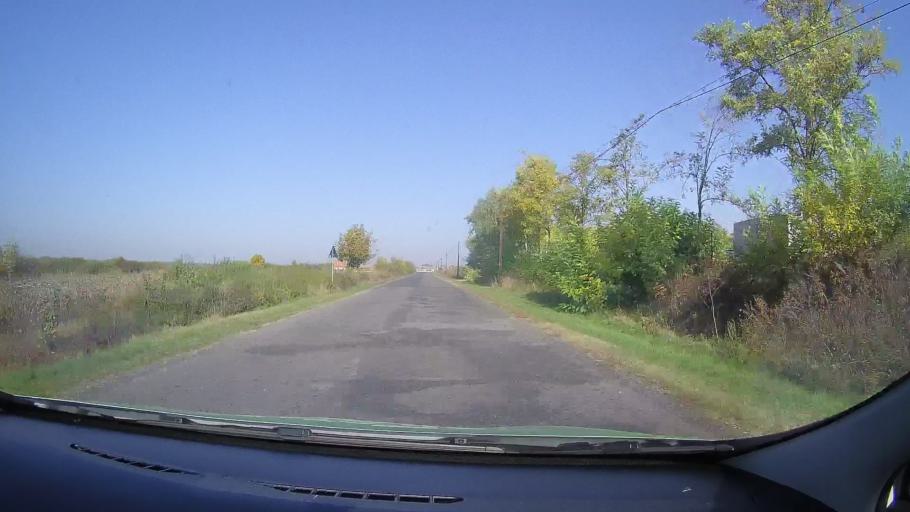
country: RO
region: Satu Mare
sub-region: Comuna Ciumesti
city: Ciumesti
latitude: 47.6497
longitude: 22.3369
